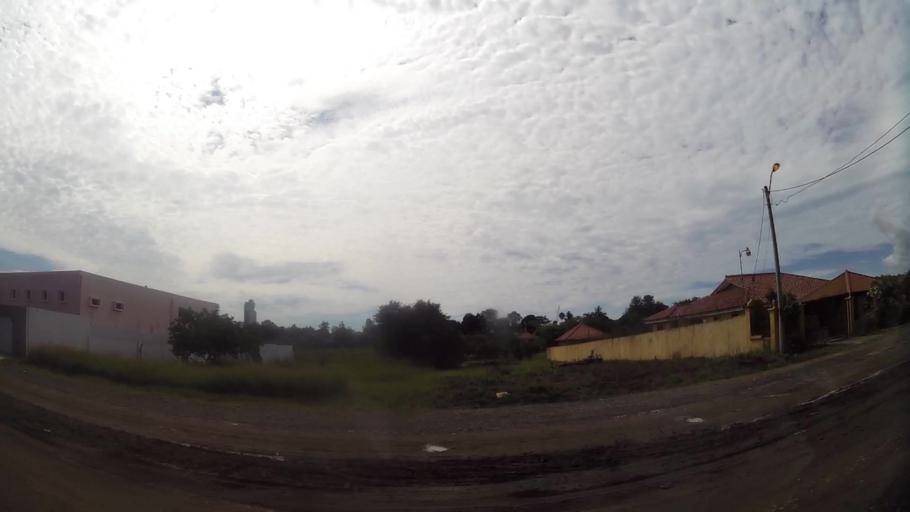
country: PA
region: Panama
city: Nueva Gorgona
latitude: 8.5462
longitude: -79.8913
